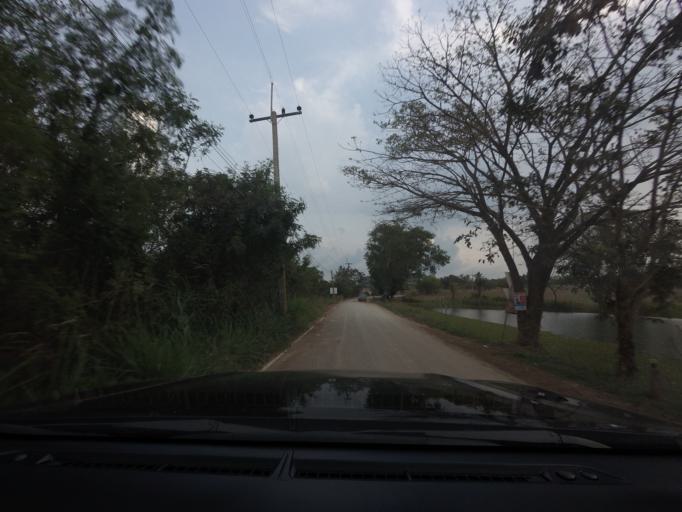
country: TH
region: Nakhon Ratchasima
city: Wang Nam Khiao
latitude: 14.3984
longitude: 101.7936
